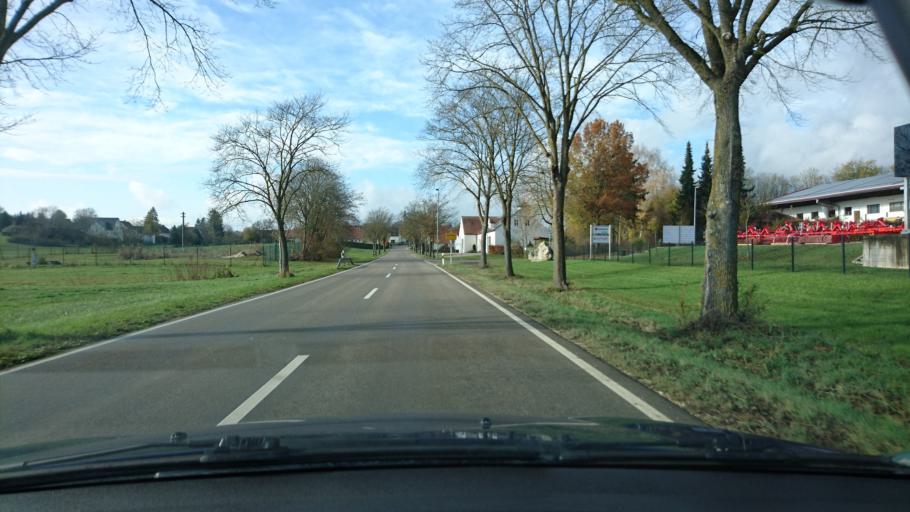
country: DE
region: Bavaria
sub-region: Swabia
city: Amerdingen
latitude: 48.7261
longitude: 10.4922
